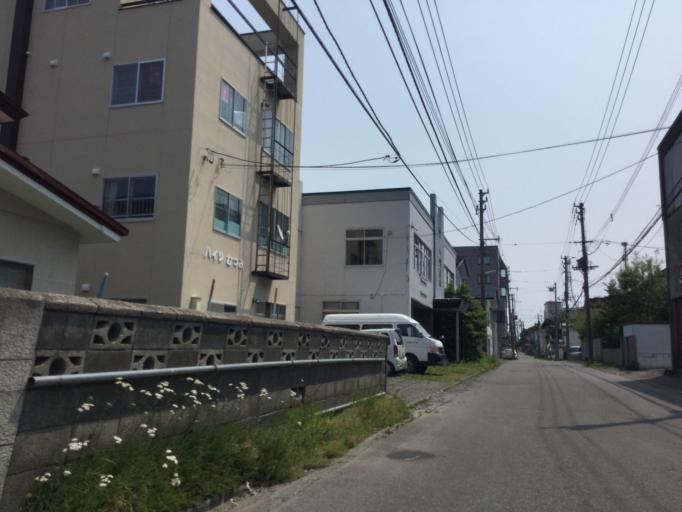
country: JP
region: Hokkaido
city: Wakkanai
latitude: 45.3998
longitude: 141.6783
